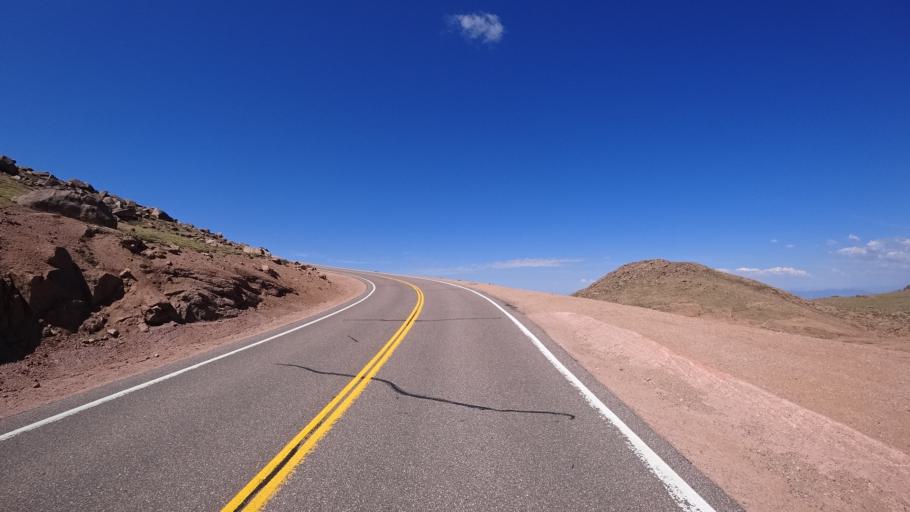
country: US
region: Colorado
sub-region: El Paso County
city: Cascade-Chipita Park
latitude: 38.8482
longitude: -105.0534
